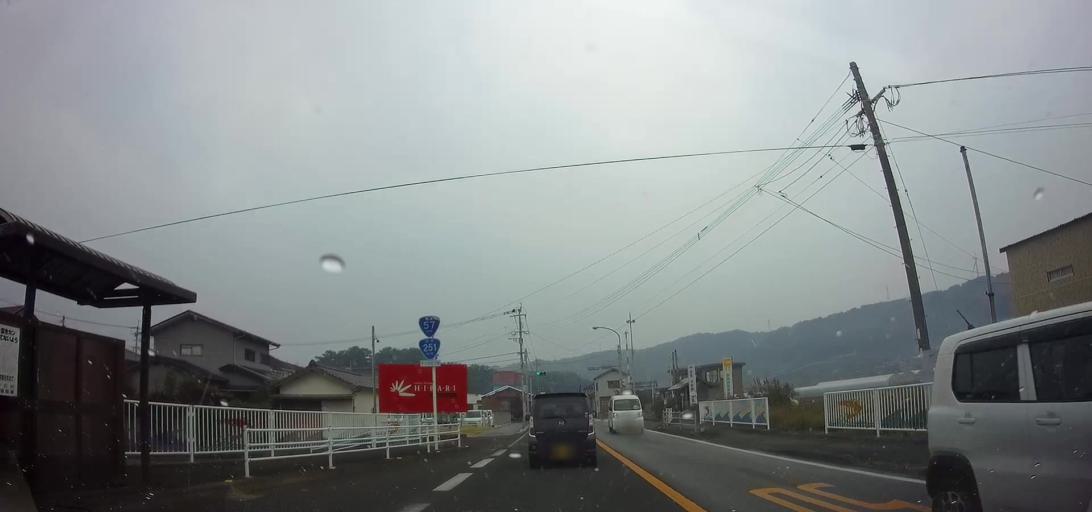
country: JP
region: Nagasaki
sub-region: Isahaya-shi
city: Isahaya
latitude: 32.7889
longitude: 130.1893
